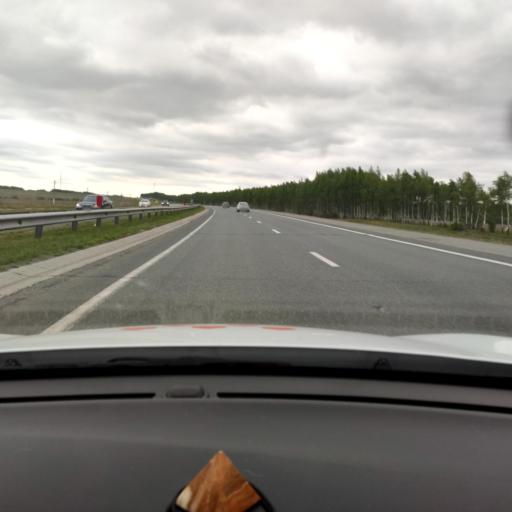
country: RU
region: Tatarstan
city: Vysokaya Gora
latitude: 55.7334
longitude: 49.4106
